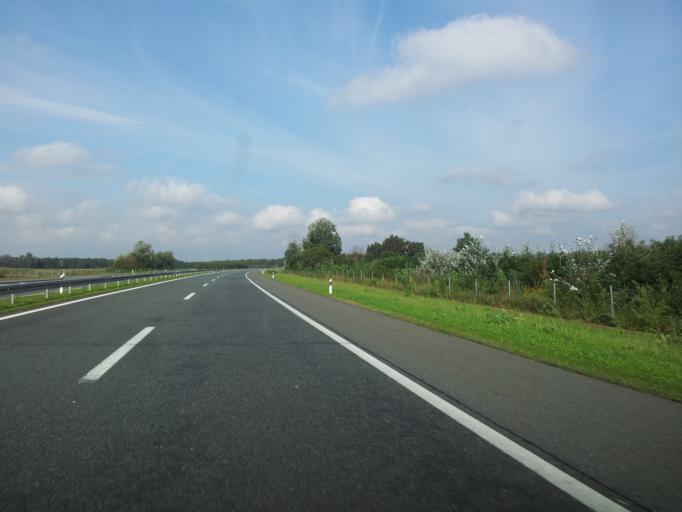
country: HR
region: Brodsko-Posavska
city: Garcin
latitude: 45.1570
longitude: 18.1870
